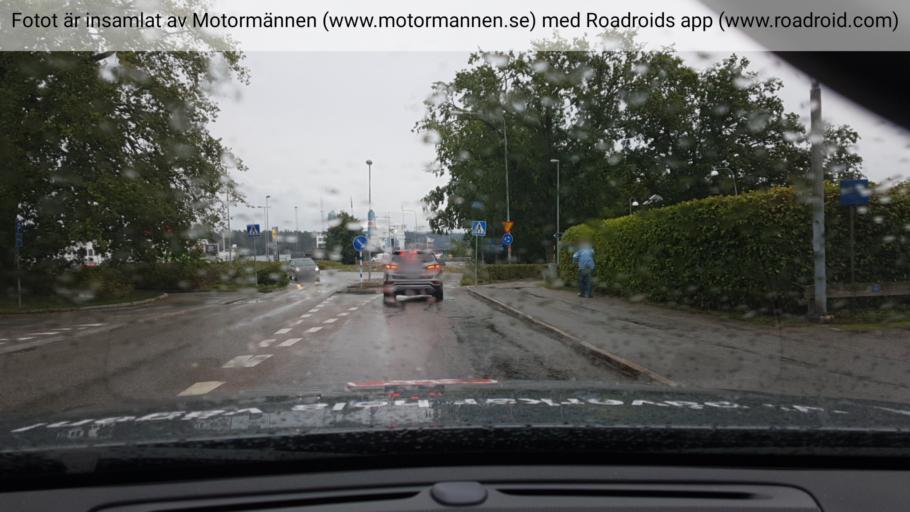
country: SE
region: Stockholm
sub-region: Nynashamns Kommun
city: Nynashamn
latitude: 58.9110
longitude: 17.9512
